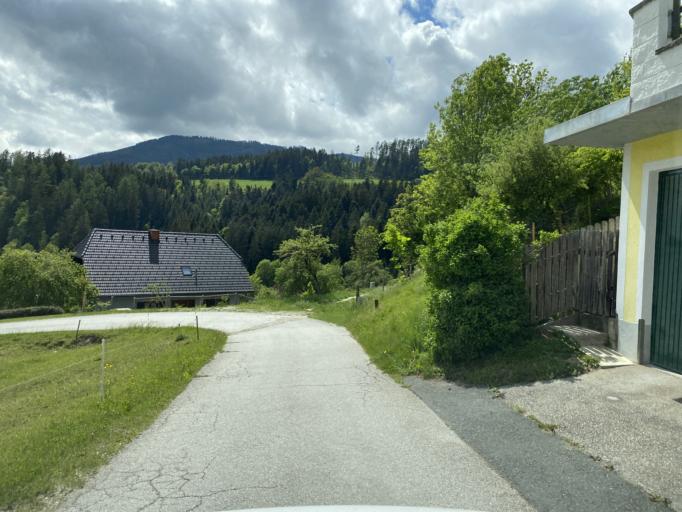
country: AT
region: Styria
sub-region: Politischer Bezirk Weiz
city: Koglhof
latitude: 47.3066
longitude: 15.6867
